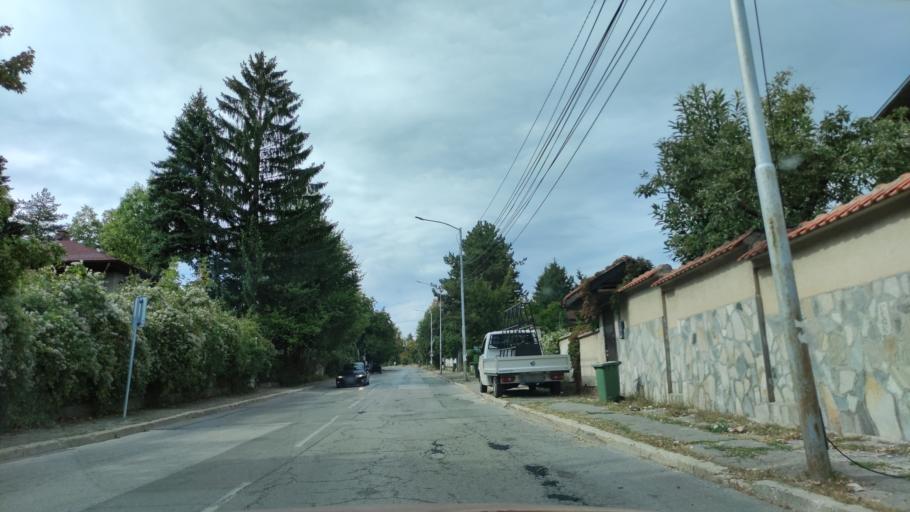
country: BG
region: Sofia-Capital
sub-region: Stolichna Obshtina
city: Sofia
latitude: 42.6492
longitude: 23.2515
